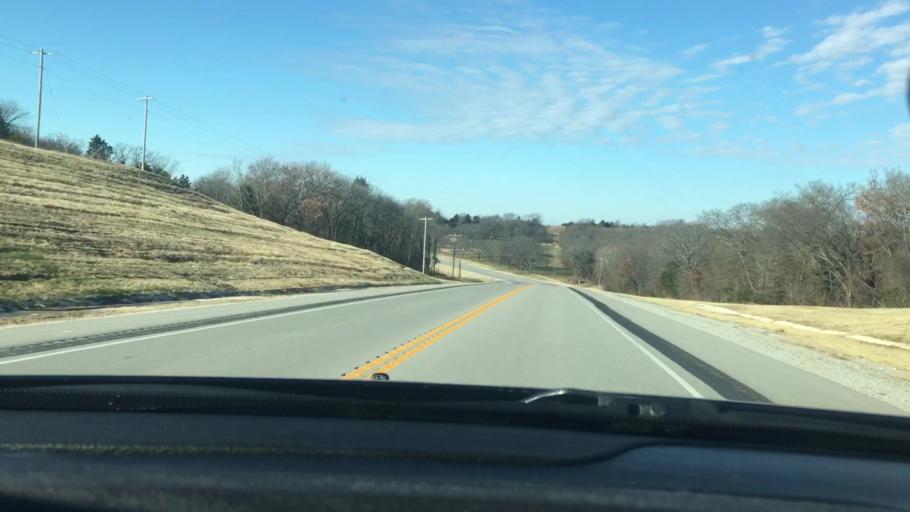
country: US
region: Oklahoma
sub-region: Love County
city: Marietta
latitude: 33.9405
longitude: -97.2543
